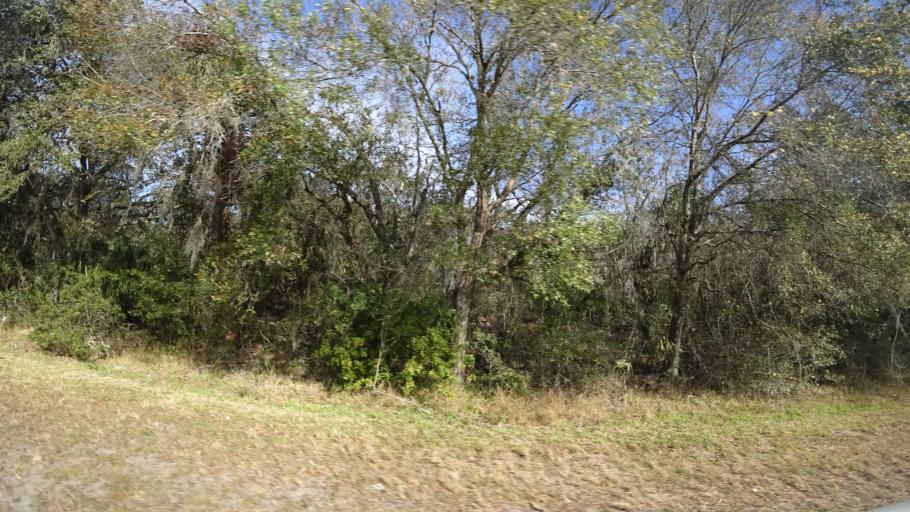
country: US
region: Florida
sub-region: Manatee County
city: Ellenton
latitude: 27.5941
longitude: -82.4506
